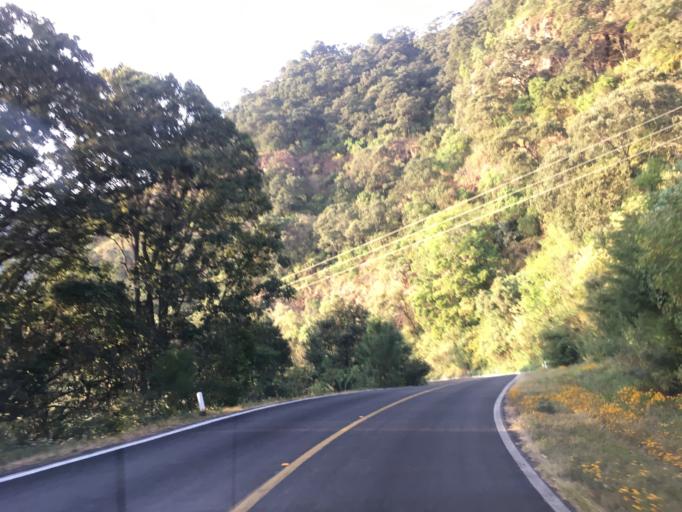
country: MX
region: Michoacan
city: Tzitzio
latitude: 19.6505
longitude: -100.9458
